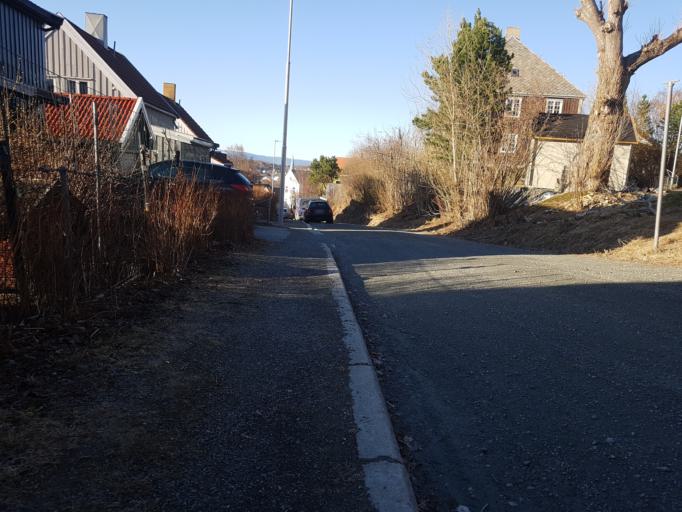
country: NO
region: Sor-Trondelag
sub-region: Trondheim
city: Trondheim
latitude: 63.4315
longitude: 10.4267
